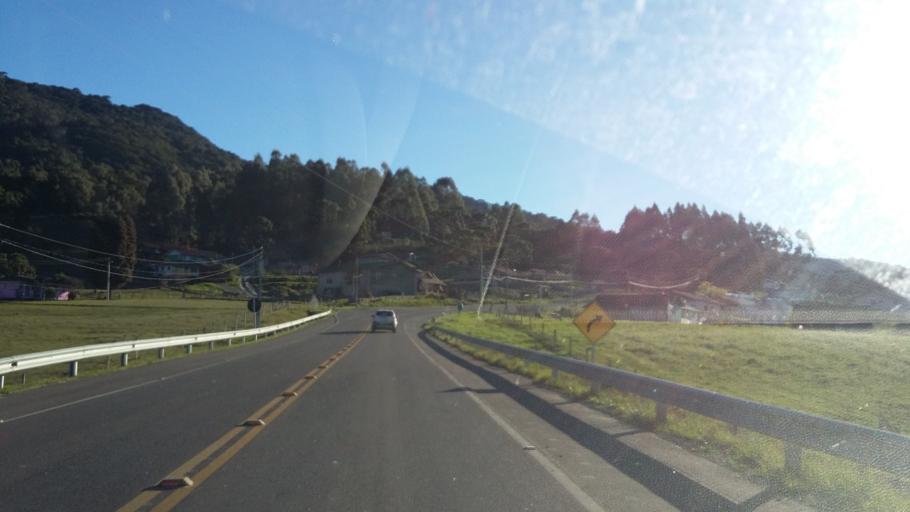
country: BR
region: Santa Catarina
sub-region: Lauro Muller
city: Lauro Muller
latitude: -28.0173
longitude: -49.5261
